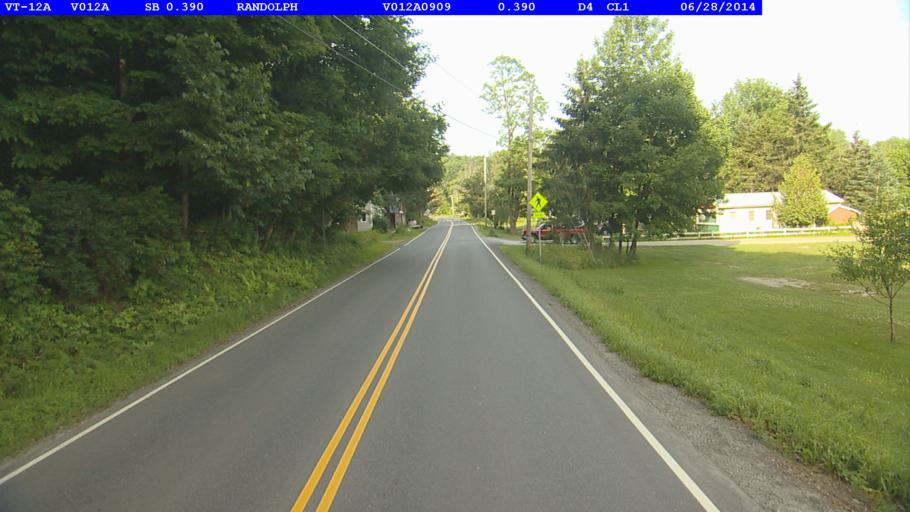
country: US
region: Vermont
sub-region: Orange County
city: Randolph
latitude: 43.9276
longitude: -72.6728
